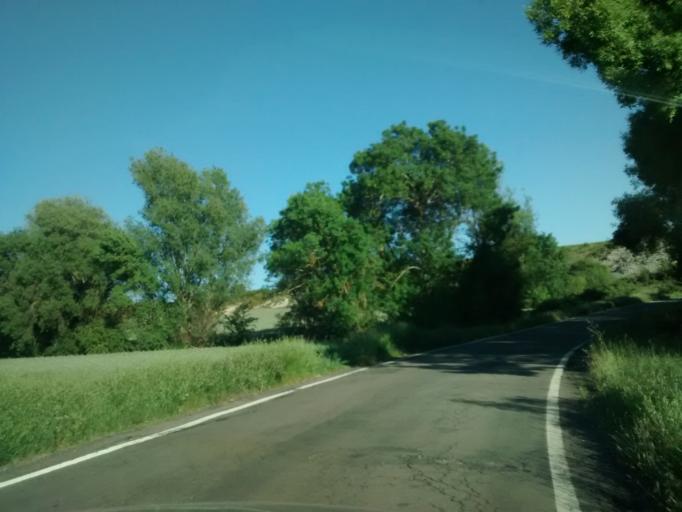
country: ES
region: Aragon
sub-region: Provincia de Huesca
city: Jaca
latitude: 42.5931
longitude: -0.6101
